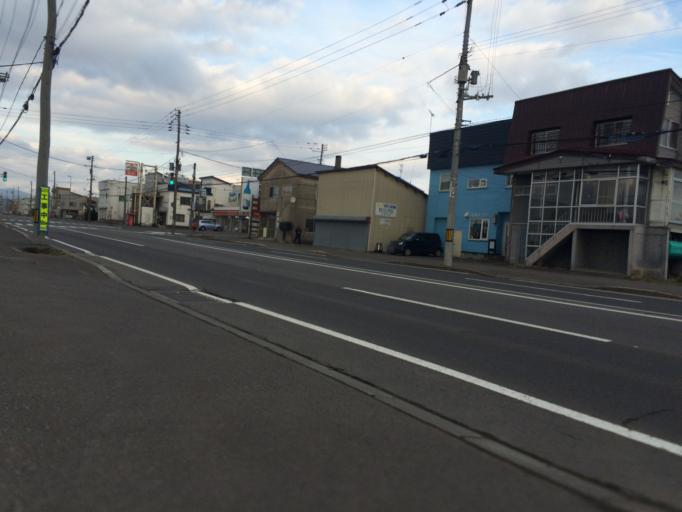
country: JP
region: Hokkaido
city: Niseko Town
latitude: 42.8944
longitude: 140.7518
